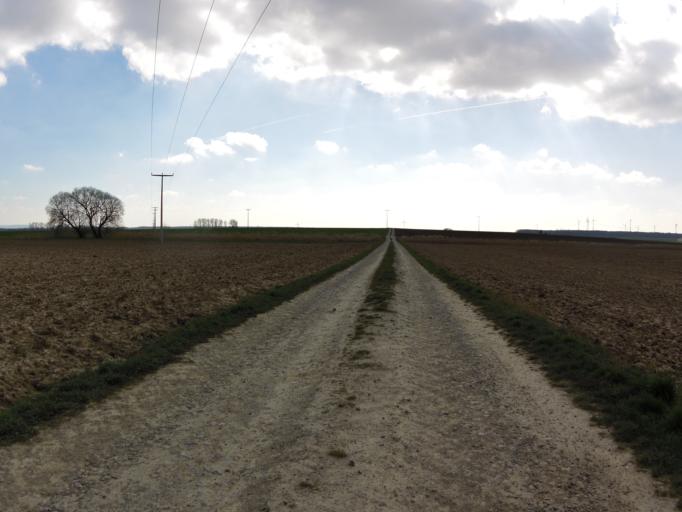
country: DE
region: Bavaria
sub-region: Regierungsbezirk Unterfranken
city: Biebelried
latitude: 49.7504
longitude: 10.0816
